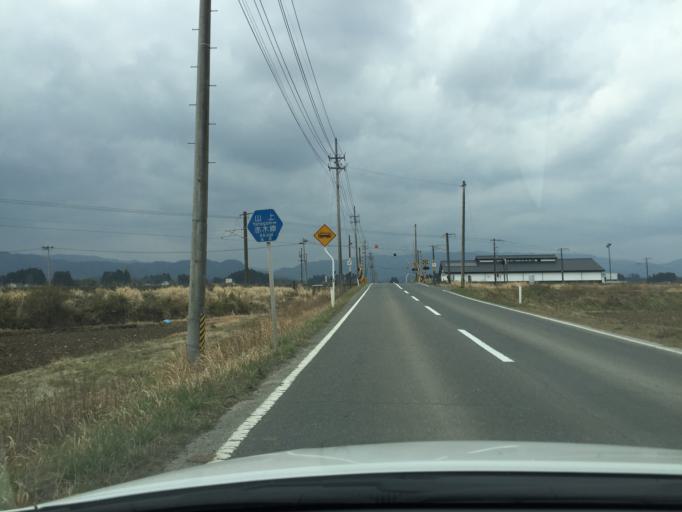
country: JP
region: Miyagi
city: Marumori
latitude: 37.7676
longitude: 140.9252
